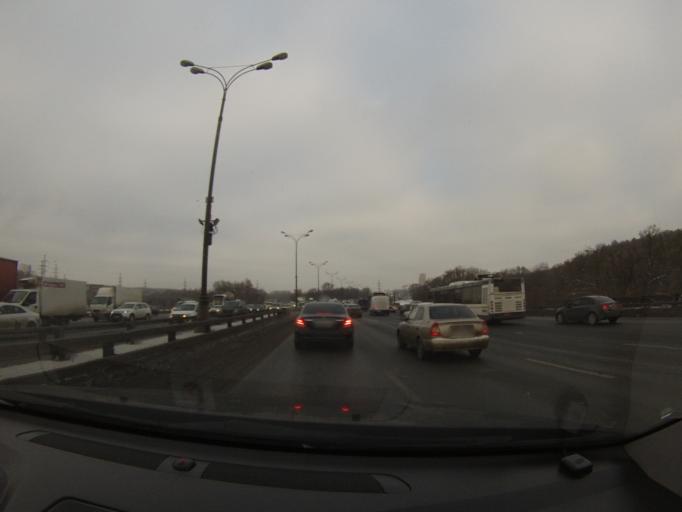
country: RU
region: Moscow
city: Strogino
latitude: 55.8433
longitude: 37.3932
